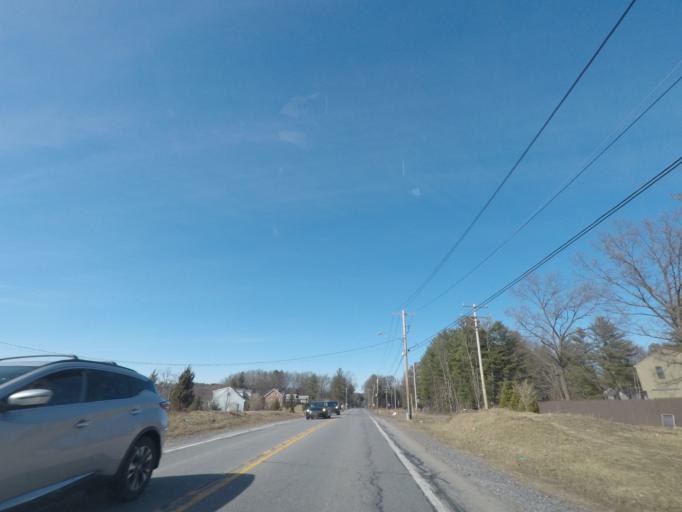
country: US
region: New York
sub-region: Saratoga County
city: Milton
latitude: 43.0579
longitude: -73.8505
